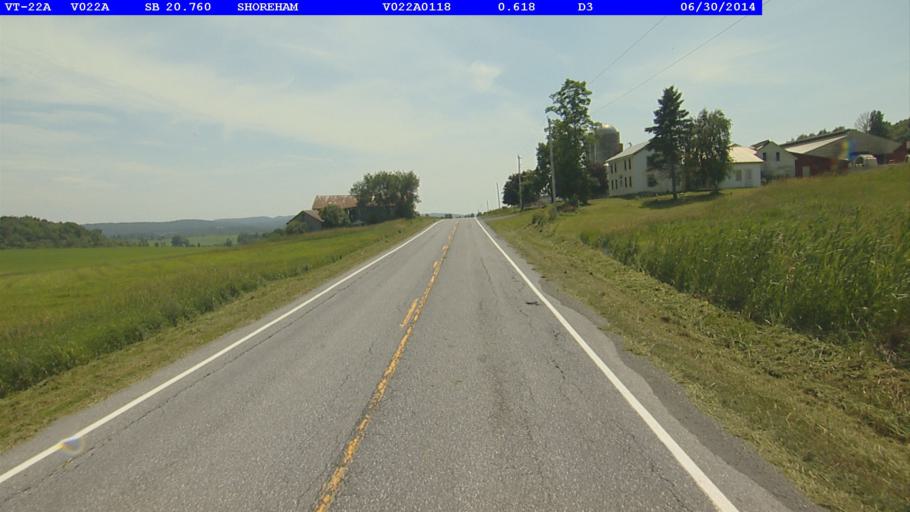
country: US
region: New York
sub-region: Essex County
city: Ticonderoga
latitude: 43.8583
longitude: -73.3094
